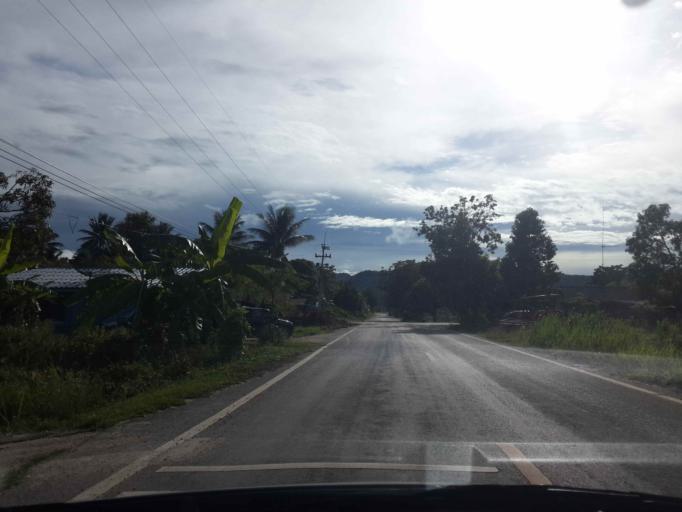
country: TH
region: Kanchanaburi
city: Dan Makham Tia
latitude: 13.8165
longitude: 99.1726
